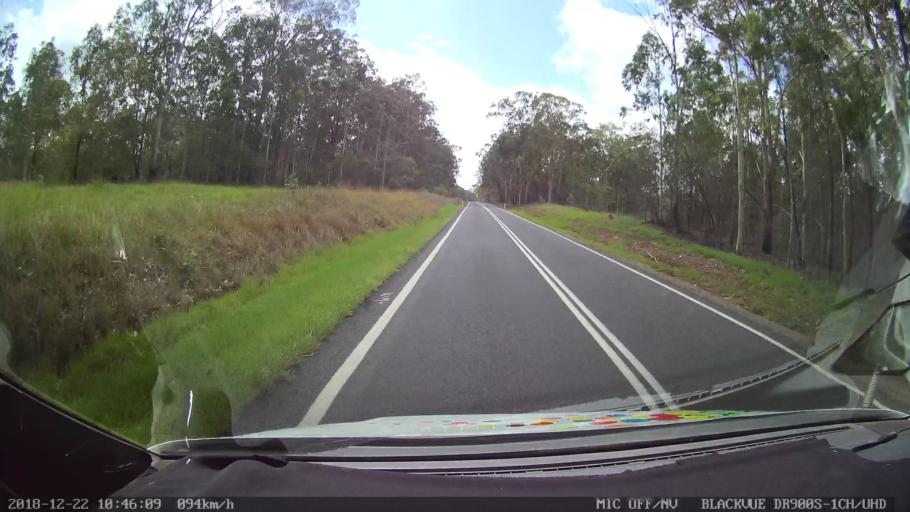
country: AU
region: New South Wales
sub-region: Clarence Valley
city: South Grafton
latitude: -29.6640
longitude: 152.8214
